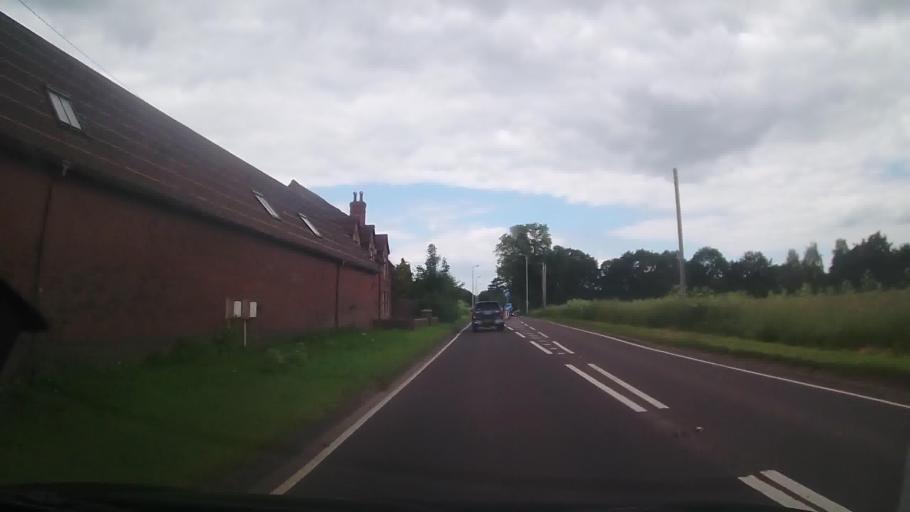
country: GB
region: England
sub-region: Herefordshire
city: Wellington
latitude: 52.1126
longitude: -2.7315
